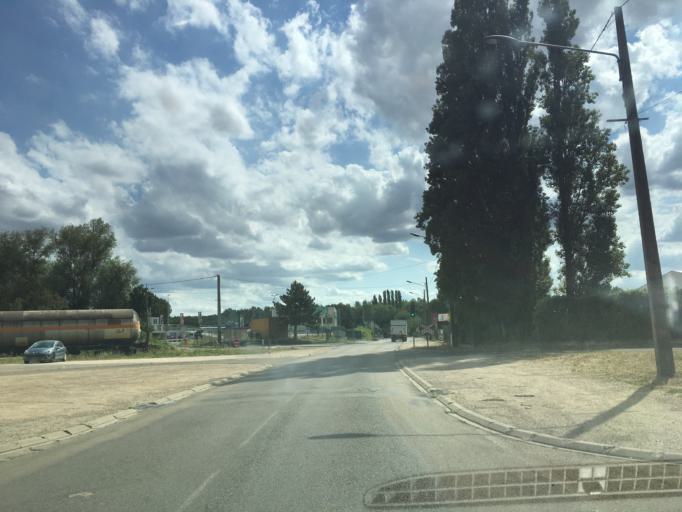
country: FR
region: Bourgogne
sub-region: Departement de l'Yonne
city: Joigny
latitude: 47.9748
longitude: 3.3857
